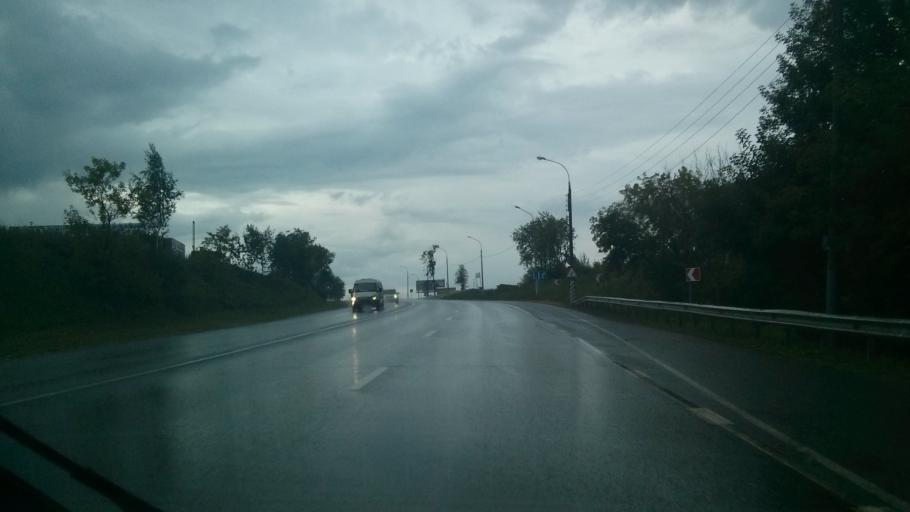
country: RU
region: Nizjnij Novgorod
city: Afonino
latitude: 56.2338
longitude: 44.0985
